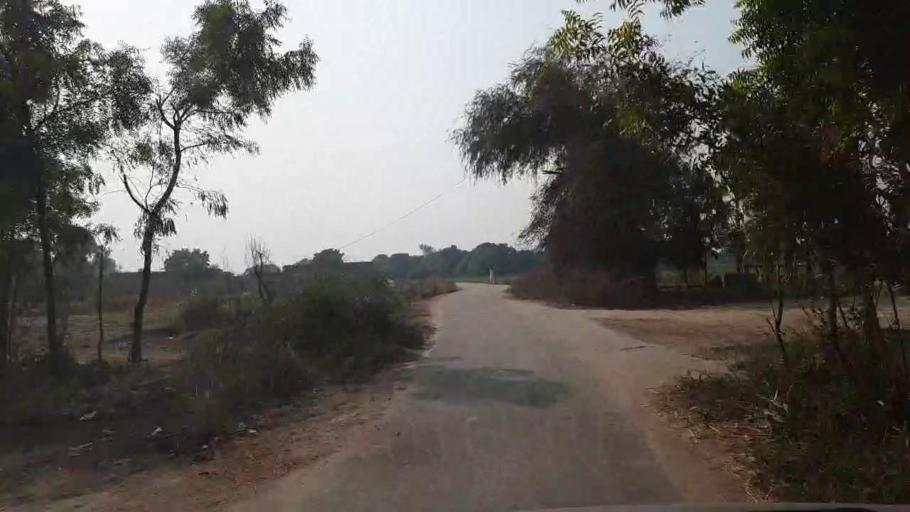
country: PK
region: Sindh
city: Bhit Shah
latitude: 25.8499
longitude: 68.5015
